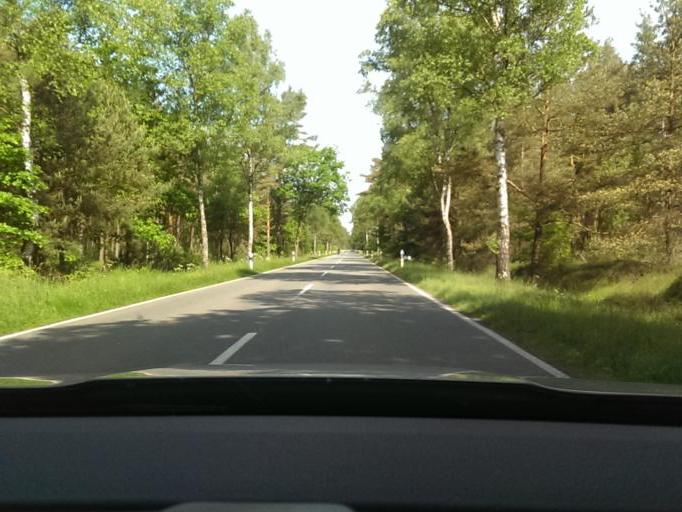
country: DE
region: Lower Saxony
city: Lindwedel
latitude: 52.6367
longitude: 9.6887
